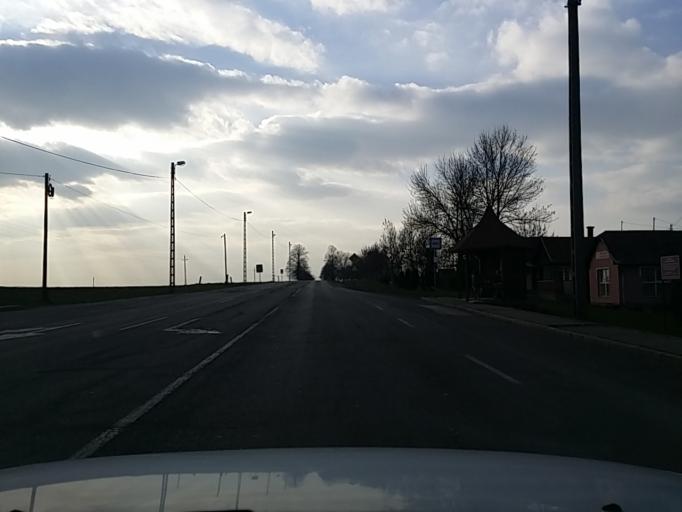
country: HU
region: Borsod-Abauj-Zemplen
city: Putnok
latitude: 48.3016
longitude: 20.3802
